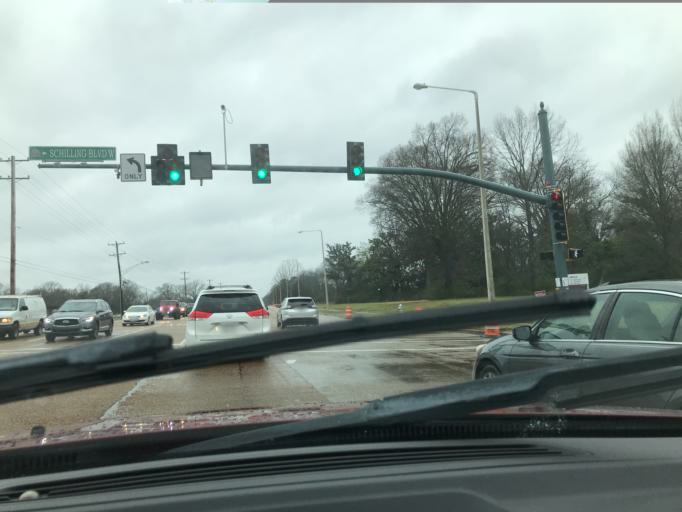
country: US
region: Tennessee
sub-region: Shelby County
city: Collierville
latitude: 35.0465
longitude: -89.7053
